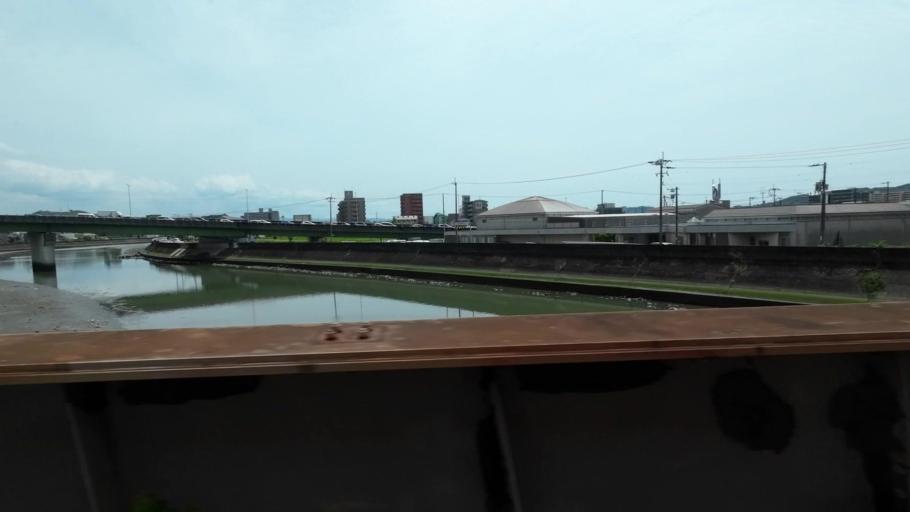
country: JP
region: Kochi
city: Kochi-shi
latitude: 33.5741
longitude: 133.5544
